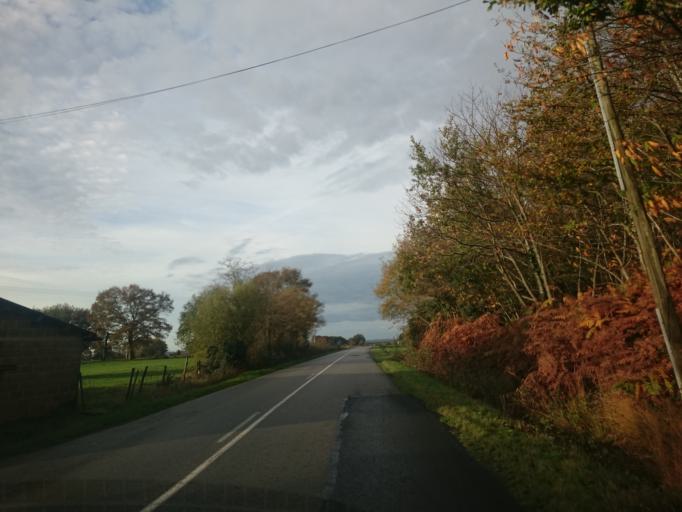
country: FR
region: Brittany
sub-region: Departement d'Ille-et-Vilaine
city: Crevin
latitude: 47.9265
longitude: -1.6882
